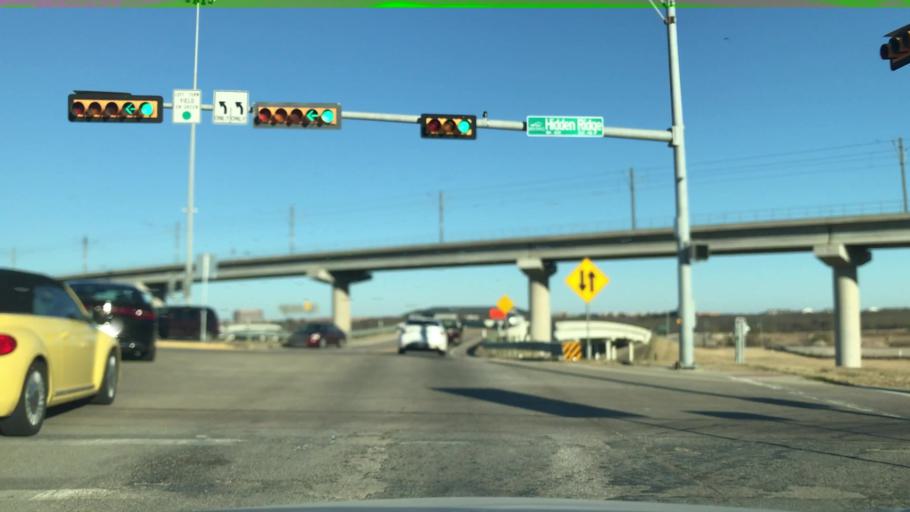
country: US
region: Texas
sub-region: Dallas County
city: Irving
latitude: 32.8798
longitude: -96.9464
